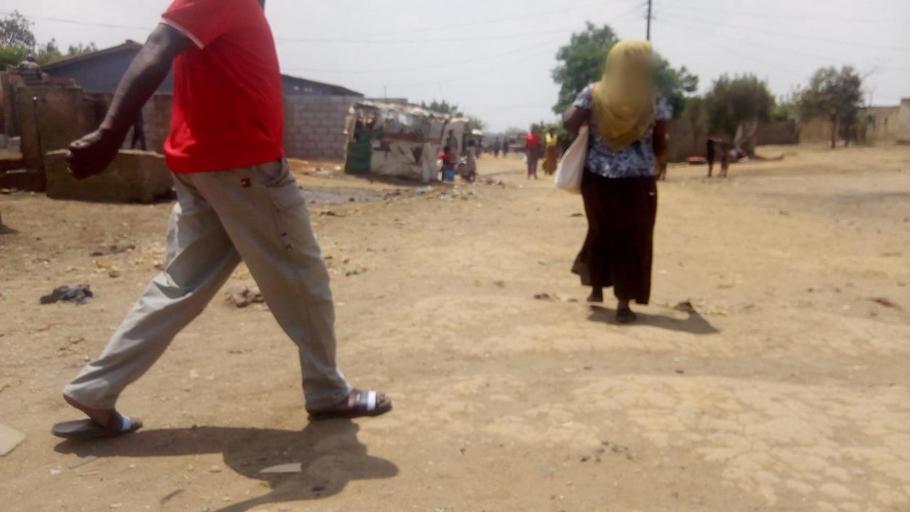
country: ZM
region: Lusaka
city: Lusaka
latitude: -15.3656
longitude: 28.2932
